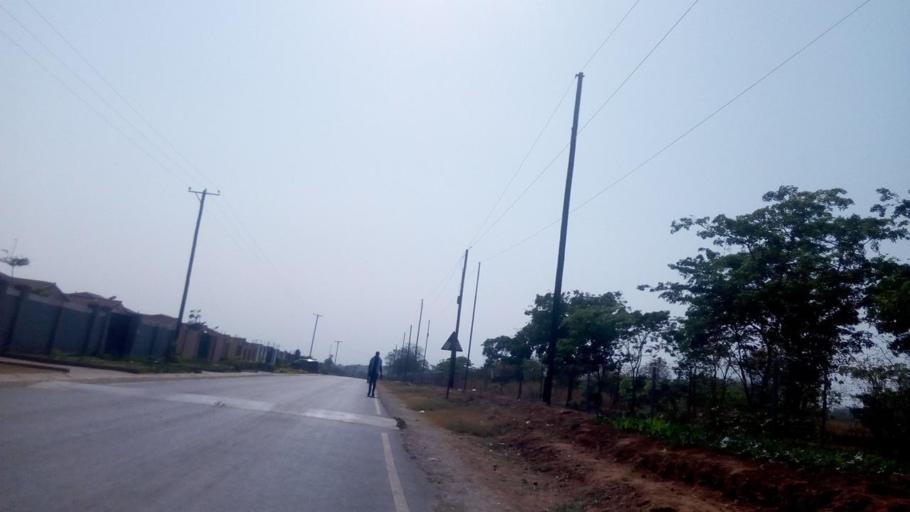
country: ZM
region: Lusaka
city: Lusaka
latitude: -15.3626
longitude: 28.2804
